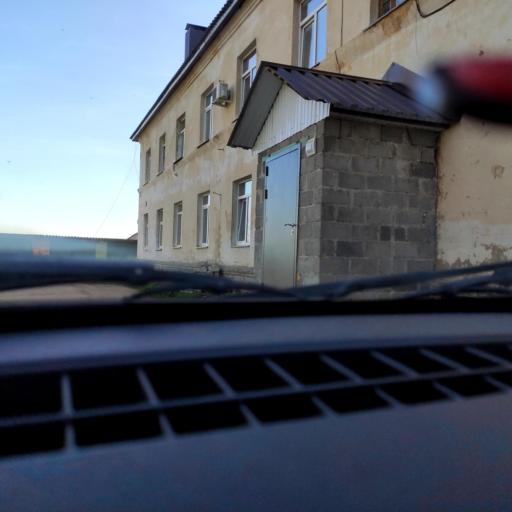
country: RU
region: Bashkortostan
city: Mikhaylovka
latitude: 54.7754
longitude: 55.8385
